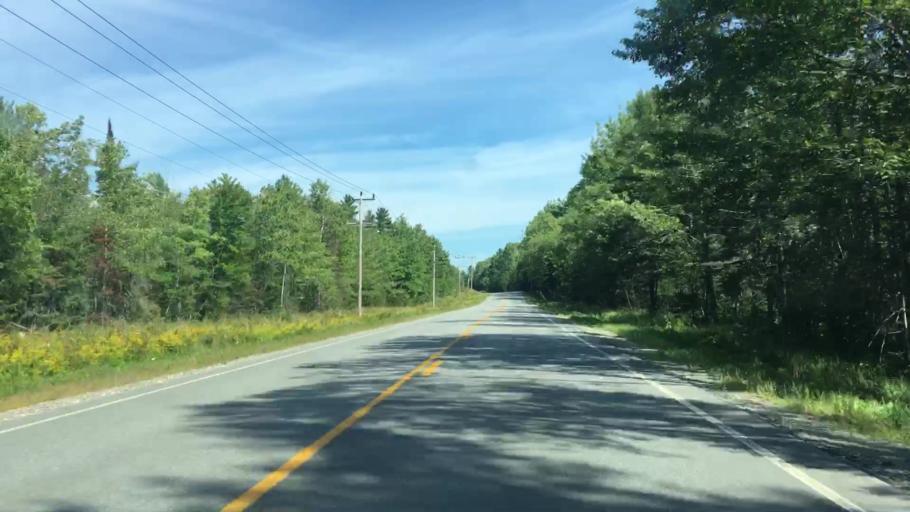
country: US
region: Maine
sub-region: Penobscot County
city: Howland
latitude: 45.2309
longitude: -68.7039
